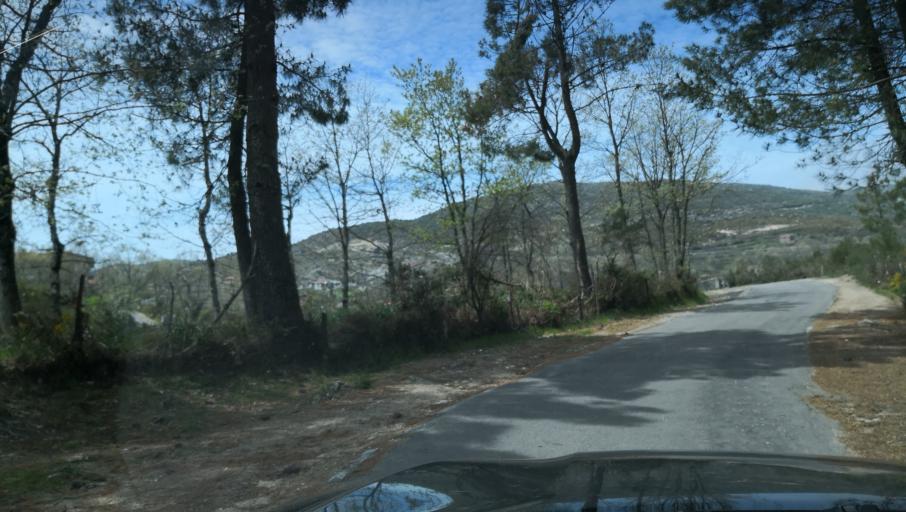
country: PT
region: Vila Real
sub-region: Vila Real
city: Vila Real
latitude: 41.3252
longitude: -7.8014
